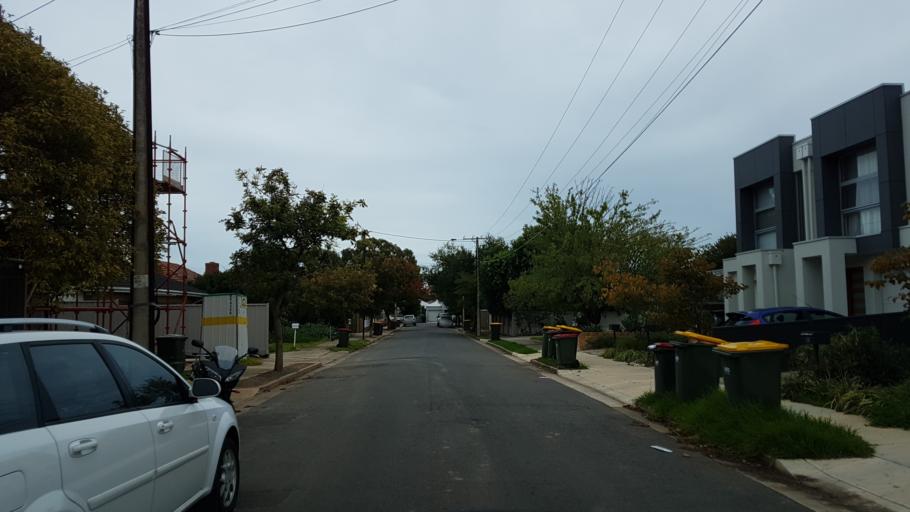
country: AU
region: South Australia
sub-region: Unley
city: Forestville
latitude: -34.9523
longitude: 138.5694
